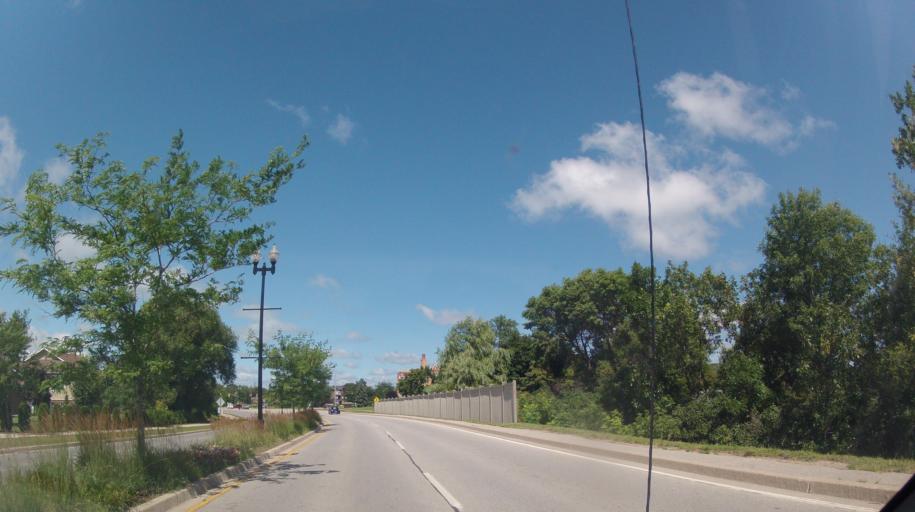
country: CA
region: Ontario
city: Collingwood
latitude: 44.5038
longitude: -80.1984
